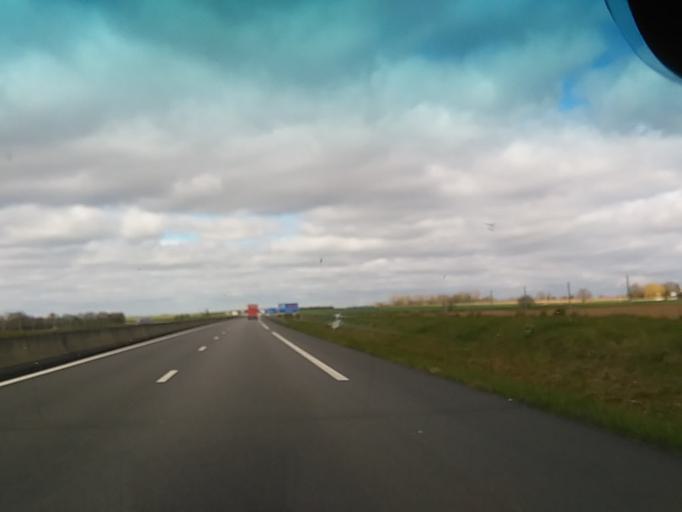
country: FR
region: Haute-Normandie
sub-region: Departement de l'Eure
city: Brionne
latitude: 49.2523
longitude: 0.7715
